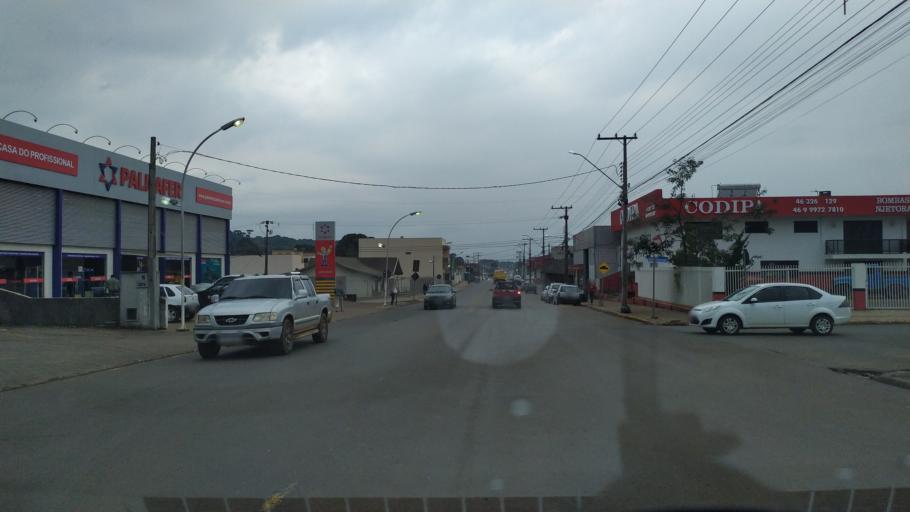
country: BR
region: Parana
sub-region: Palmas
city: Palmas
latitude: -26.4884
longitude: -51.9981
